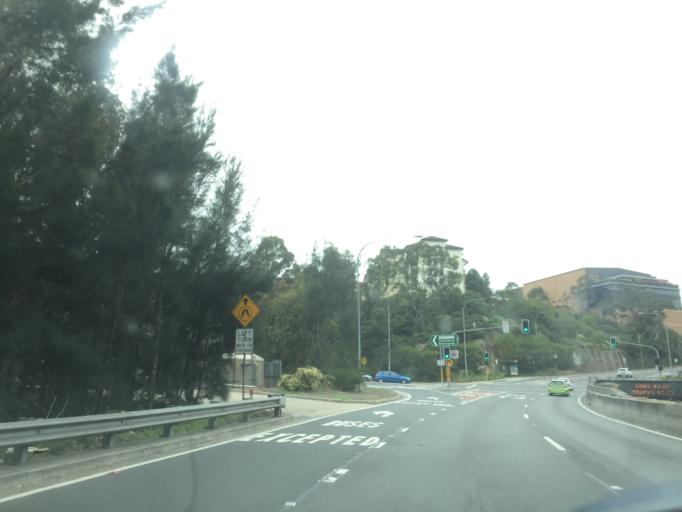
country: AU
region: New South Wales
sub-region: Ryde
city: East Ryde
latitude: -33.8011
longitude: 151.1447
